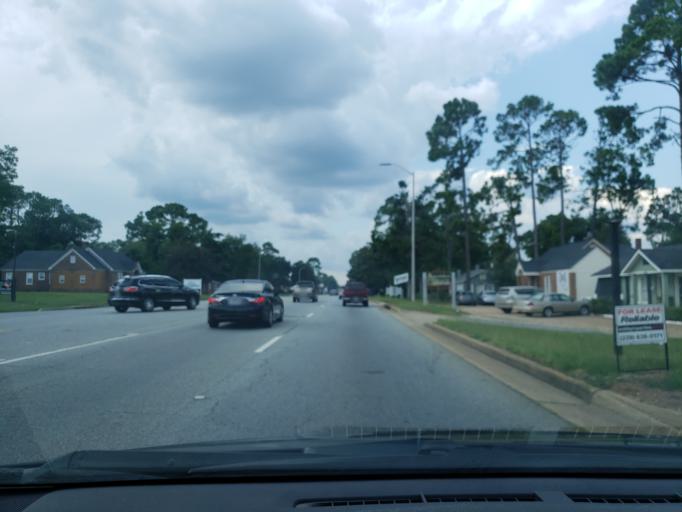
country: US
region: Georgia
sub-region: Dougherty County
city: Albany
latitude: 31.5825
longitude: -84.1777
